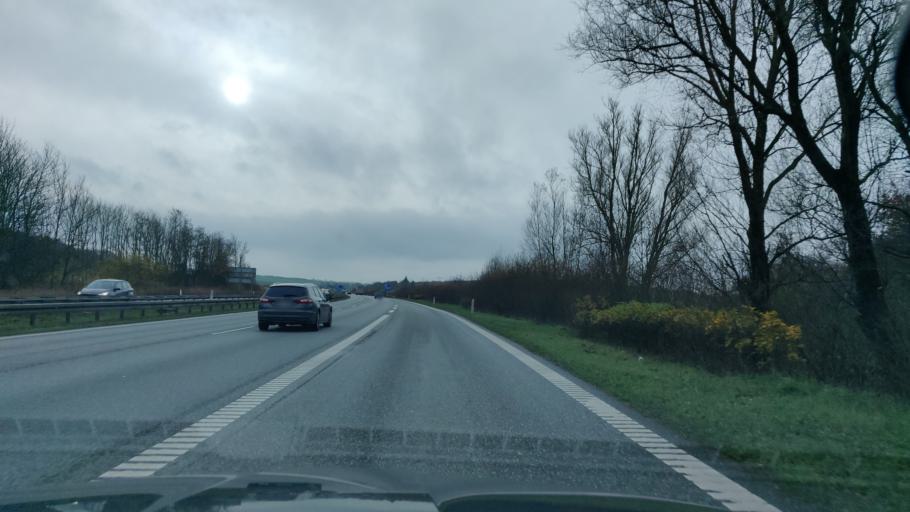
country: DK
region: North Denmark
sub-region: Alborg Kommune
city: Aalborg
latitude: 57.0049
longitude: 9.9104
